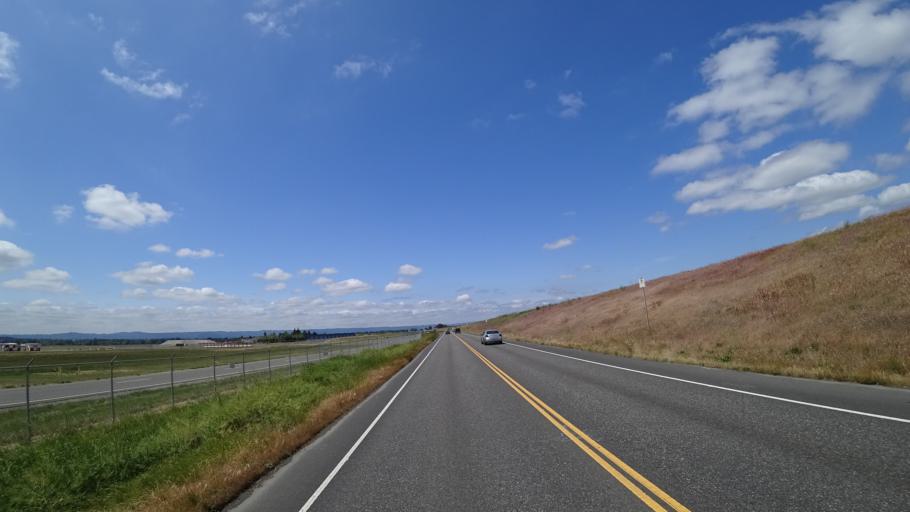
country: US
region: Washington
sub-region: Clark County
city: Walnut Grove
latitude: 45.5985
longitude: -122.6016
